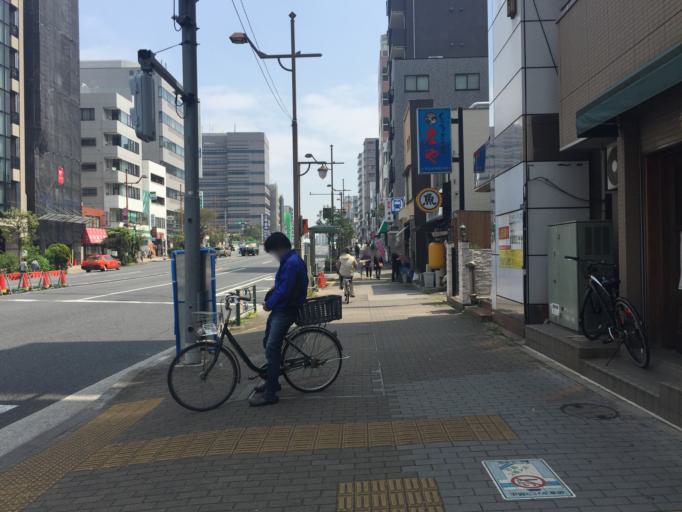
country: JP
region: Tokyo
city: Urayasu
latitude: 35.6692
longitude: 139.8070
